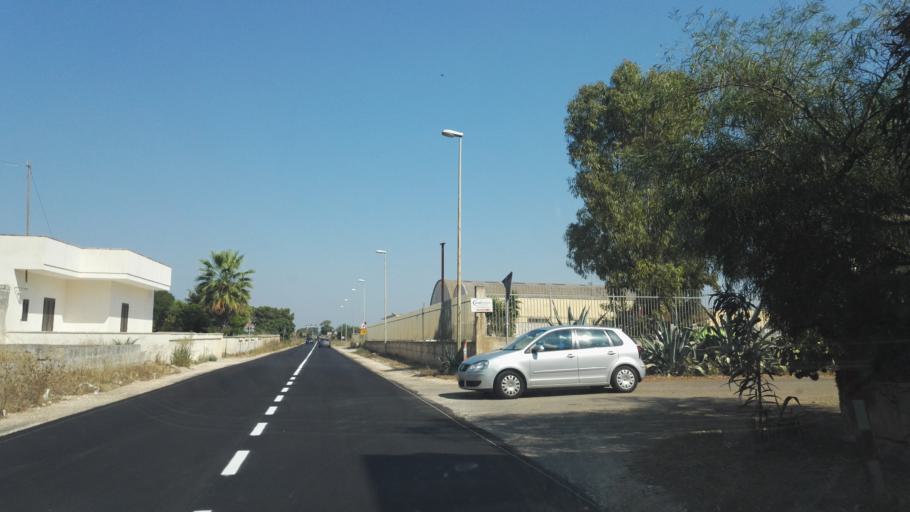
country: IT
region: Apulia
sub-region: Provincia di Lecce
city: Nardo
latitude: 40.2025
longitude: 17.9573
